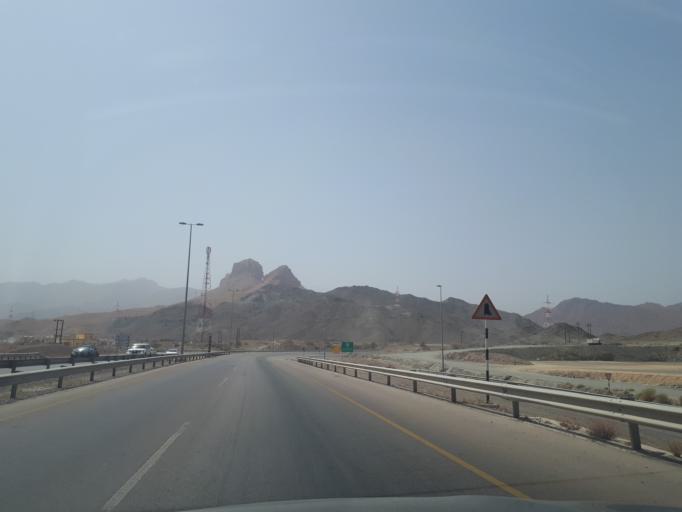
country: OM
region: Muhafazat ad Dakhiliyah
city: Bidbid
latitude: 23.4847
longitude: 58.1979
